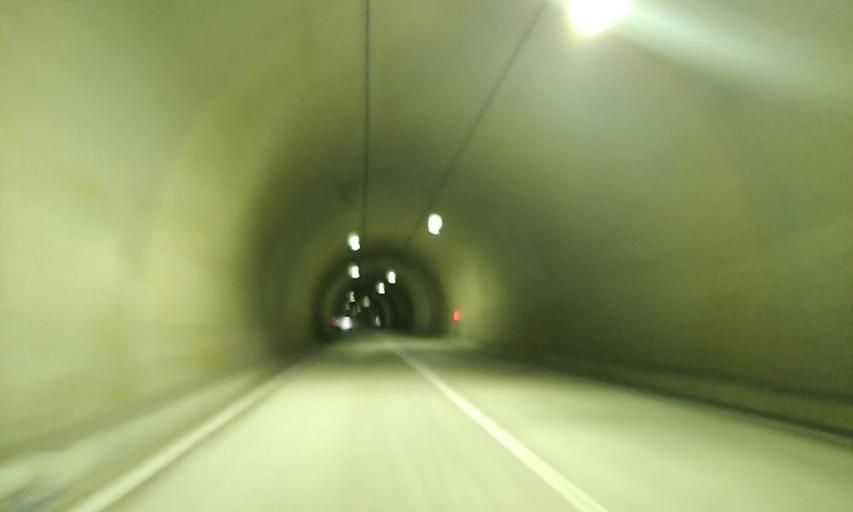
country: JP
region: Wakayama
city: Shingu
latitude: 33.8808
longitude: 135.8774
